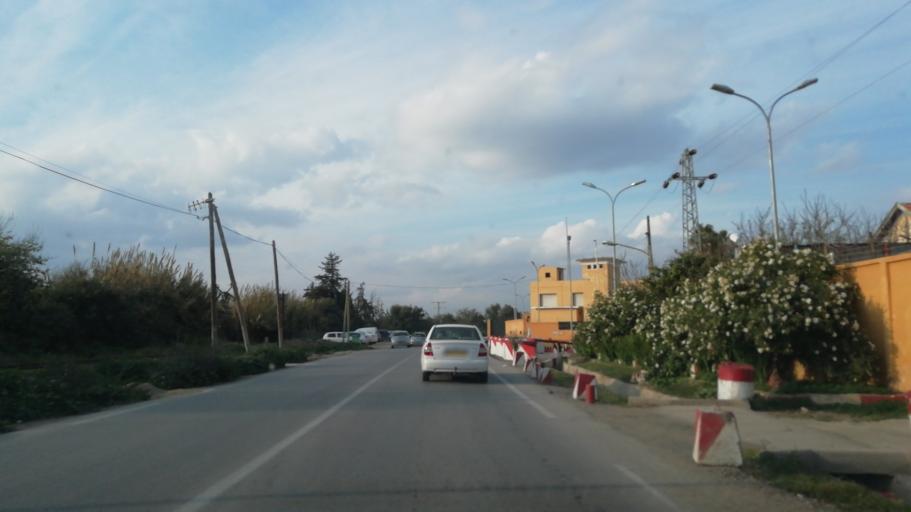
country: DZ
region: Mascara
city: Mascara
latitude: 35.5988
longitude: 0.0536
